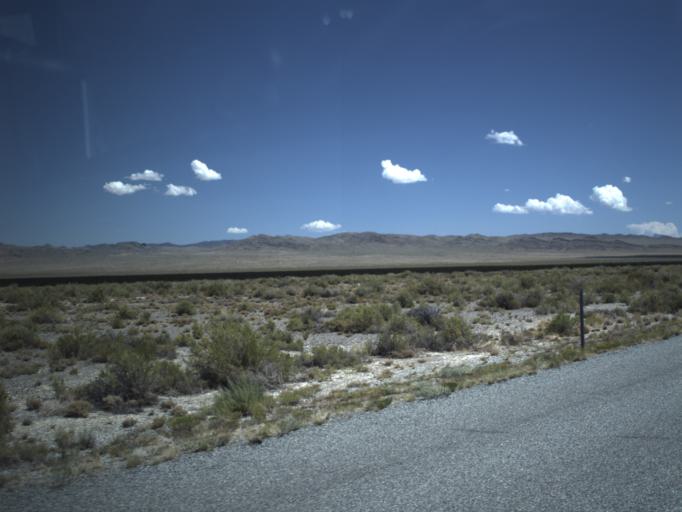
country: US
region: Nevada
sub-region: White Pine County
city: McGill
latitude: 39.0500
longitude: -113.9561
